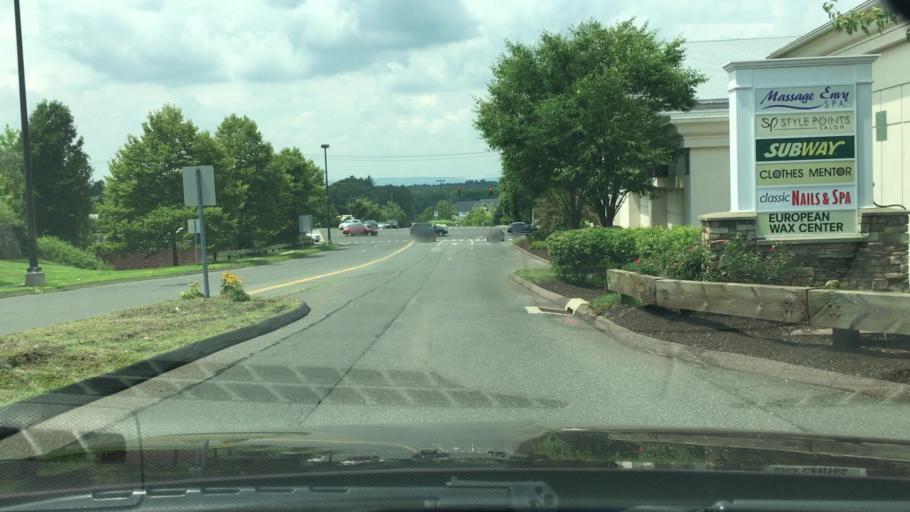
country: US
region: Connecticut
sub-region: Hartford County
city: Manchester
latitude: 41.8103
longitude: -72.5534
